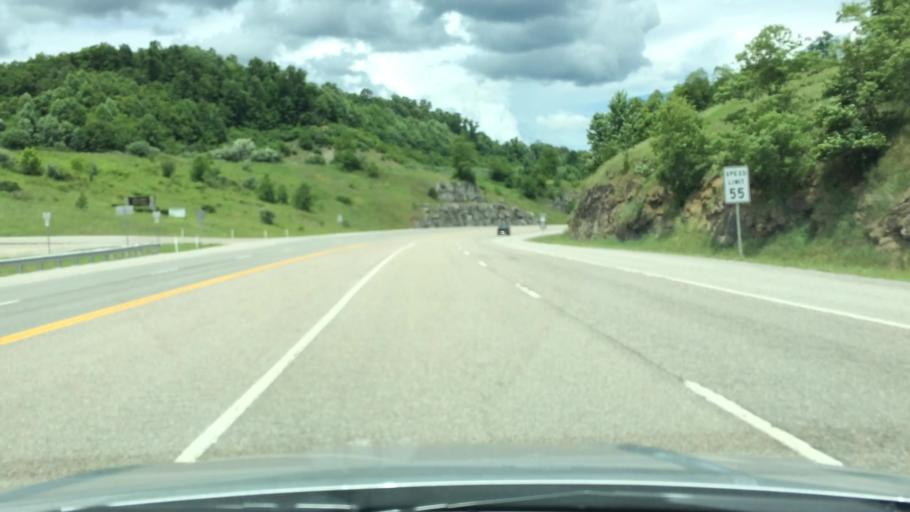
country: US
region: Kentucky
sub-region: Letcher County
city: Jenkins
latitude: 37.1660
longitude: -82.6464
